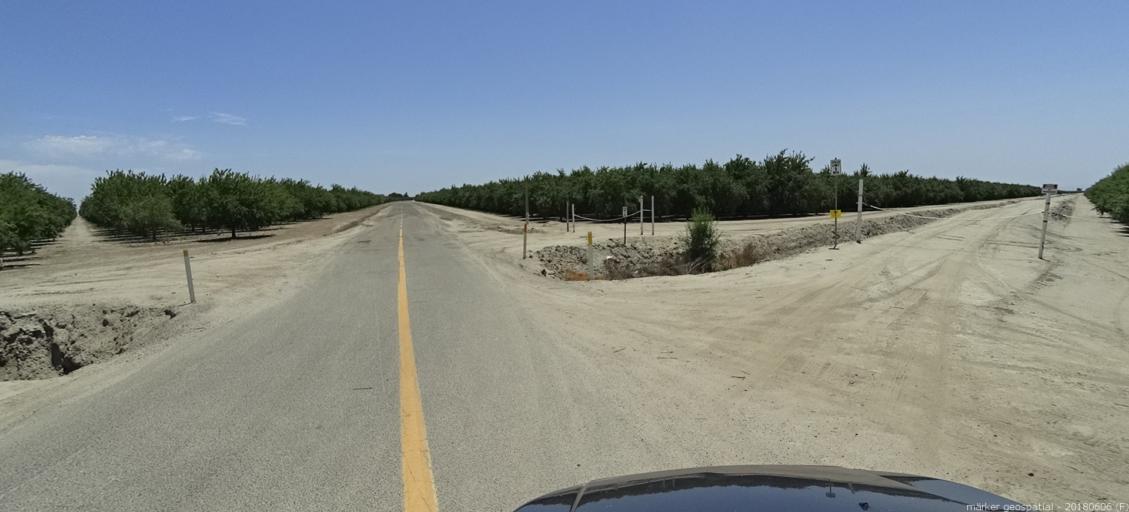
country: US
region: California
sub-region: Fresno County
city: Mendota
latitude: 36.8114
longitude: -120.3655
